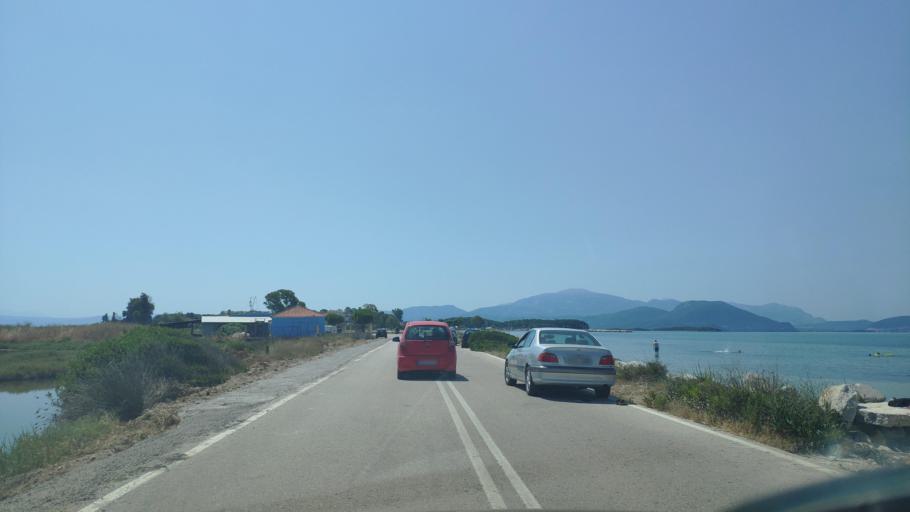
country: GR
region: Epirus
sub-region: Nomos Artas
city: Aneza
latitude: 39.0214
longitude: 20.9106
